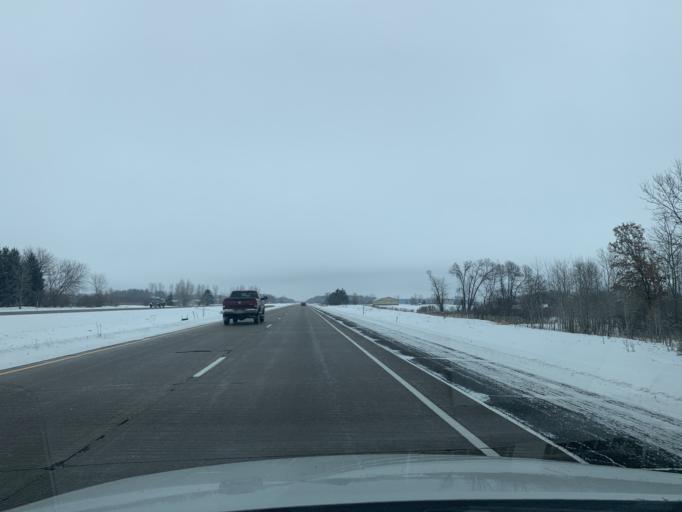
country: US
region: Minnesota
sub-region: Chisago County
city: Rush City
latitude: 45.6392
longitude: -92.9921
